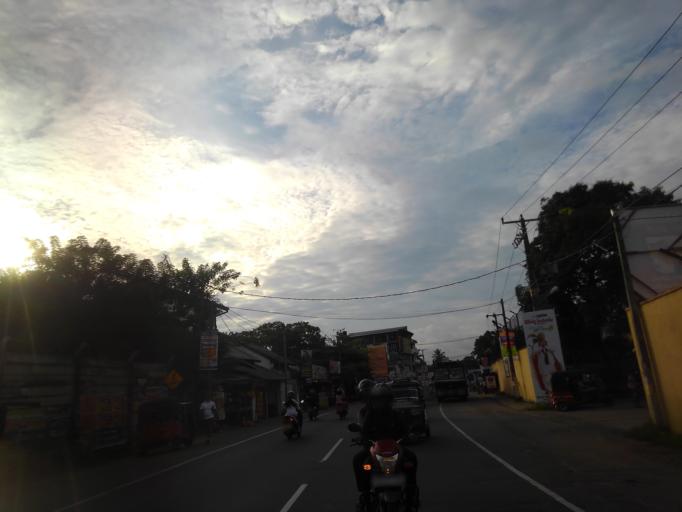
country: LK
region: Southern
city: Unawatuna
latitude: 6.0339
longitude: 80.2360
